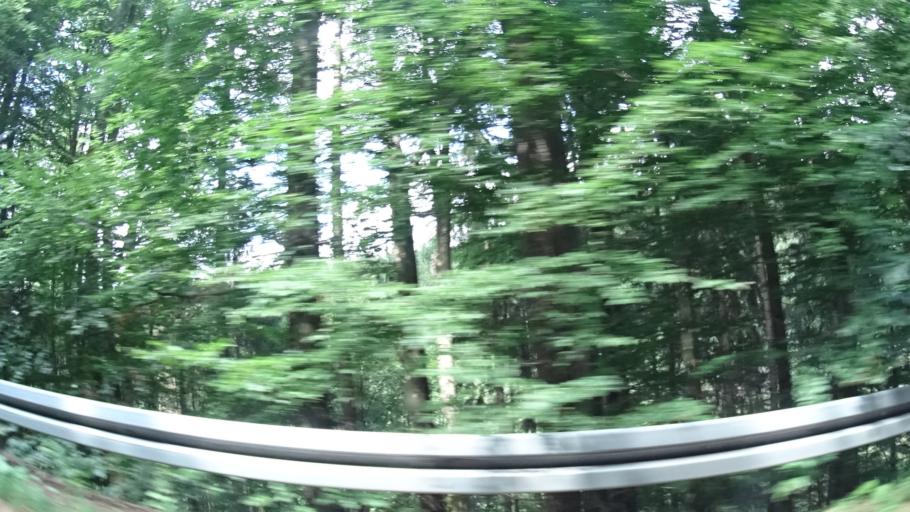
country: DE
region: Thuringia
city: Eisfeld
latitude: 50.4862
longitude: 10.9213
